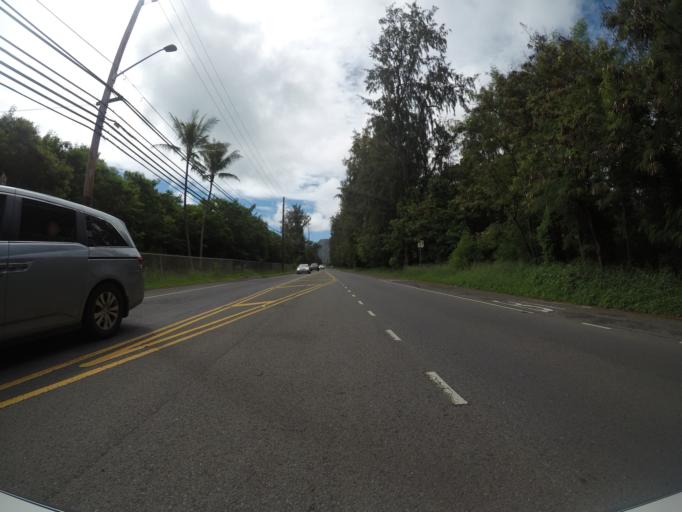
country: US
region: Hawaii
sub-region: Honolulu County
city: Waimanalo Beach
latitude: 21.3429
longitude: -157.7073
